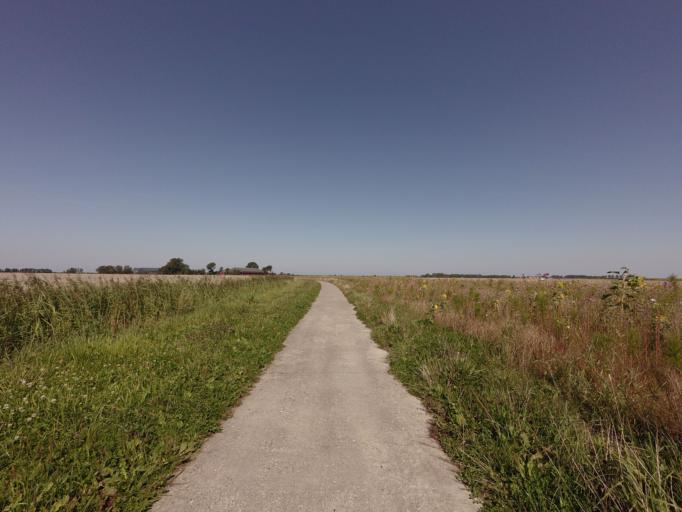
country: NL
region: Friesland
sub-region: Gemeente Dongeradeel
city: Anjum
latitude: 53.3885
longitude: 6.0661
